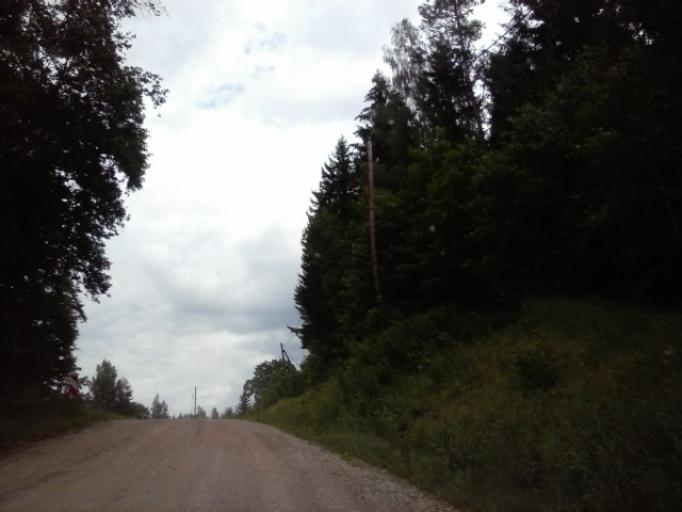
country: EE
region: Vorumaa
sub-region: Voru linn
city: Voru
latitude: 57.7446
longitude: 27.0844
